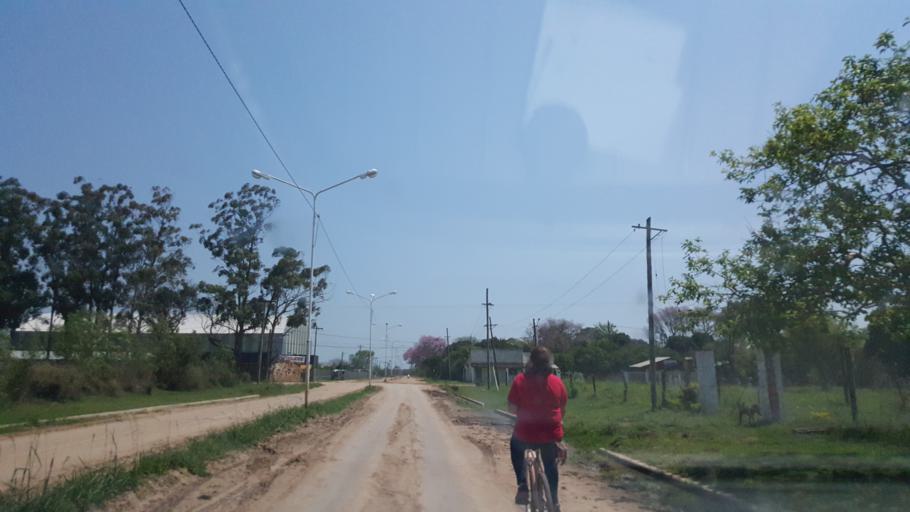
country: AR
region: Corrientes
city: Ita Ibate
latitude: -27.4287
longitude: -57.3416
